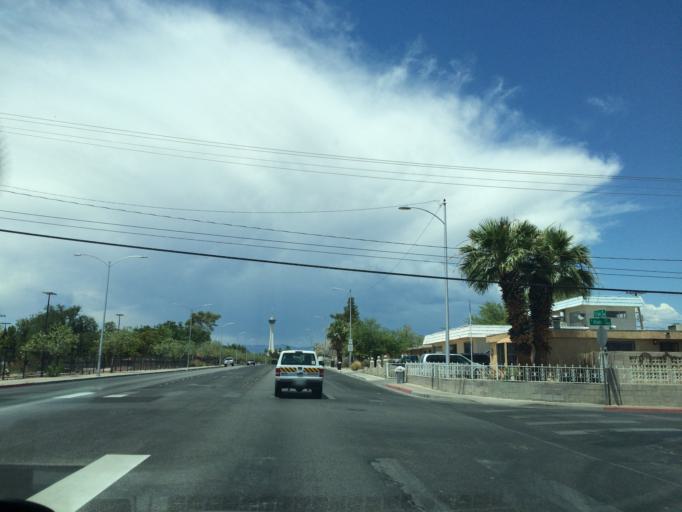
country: US
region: Nevada
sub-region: Clark County
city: Winchester
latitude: 36.1481
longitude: -115.1142
